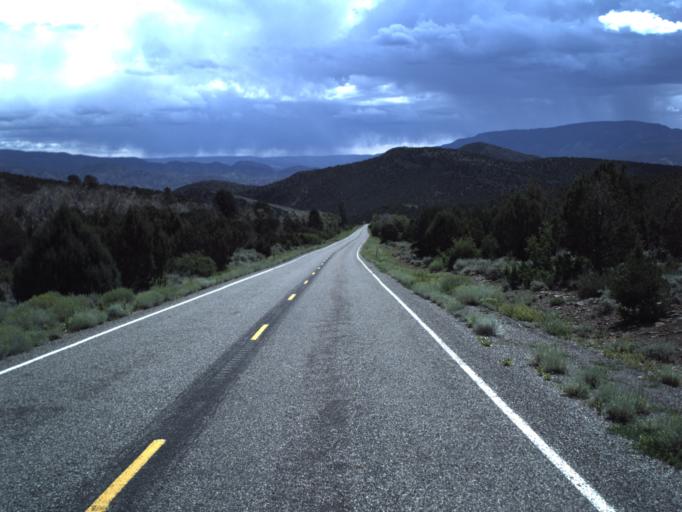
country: US
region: Utah
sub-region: Piute County
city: Junction
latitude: 38.2634
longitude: -112.2995
